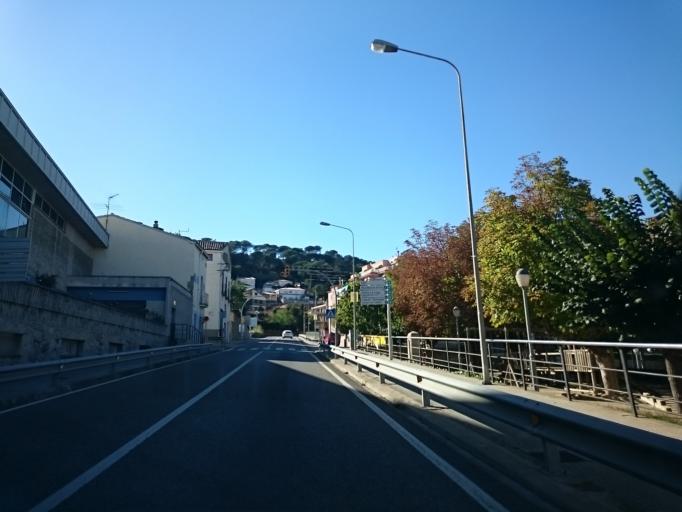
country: ES
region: Catalonia
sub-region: Provincia de Barcelona
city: Capellades
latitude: 41.5274
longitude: 1.6843
